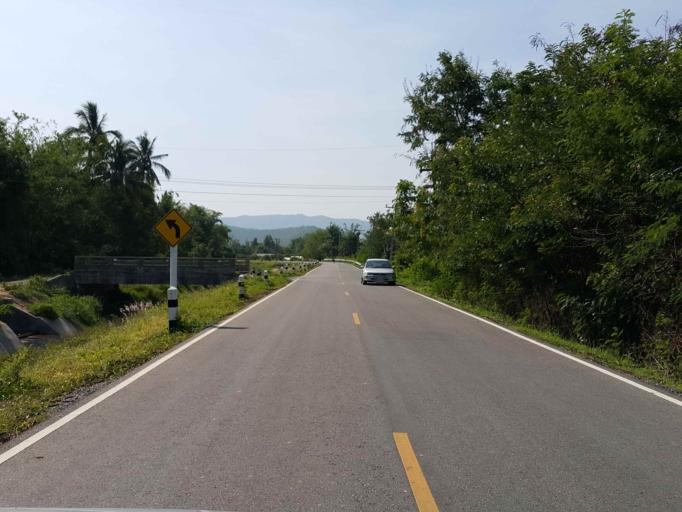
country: TH
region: Chiang Mai
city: Mae On
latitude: 18.8082
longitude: 99.1776
